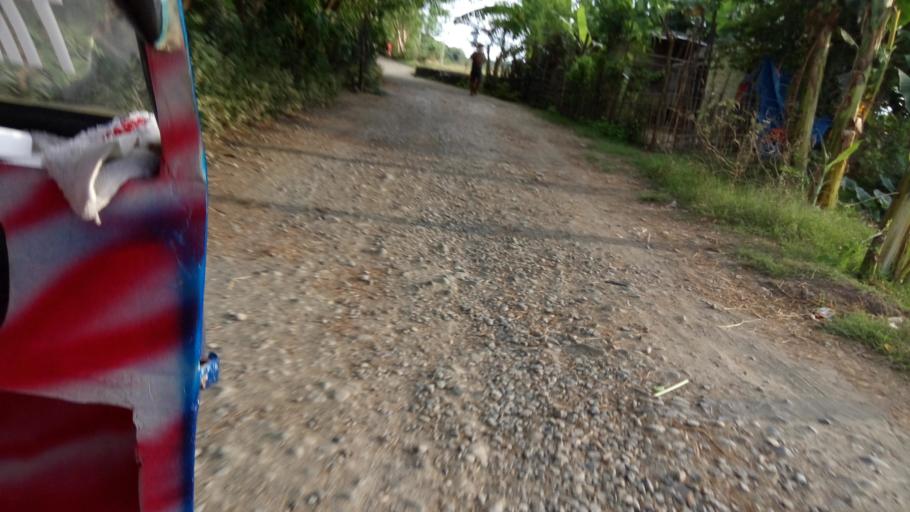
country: PH
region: Ilocos
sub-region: Province of La Union
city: Santo Tomas
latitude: 16.2819
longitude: 120.3848
